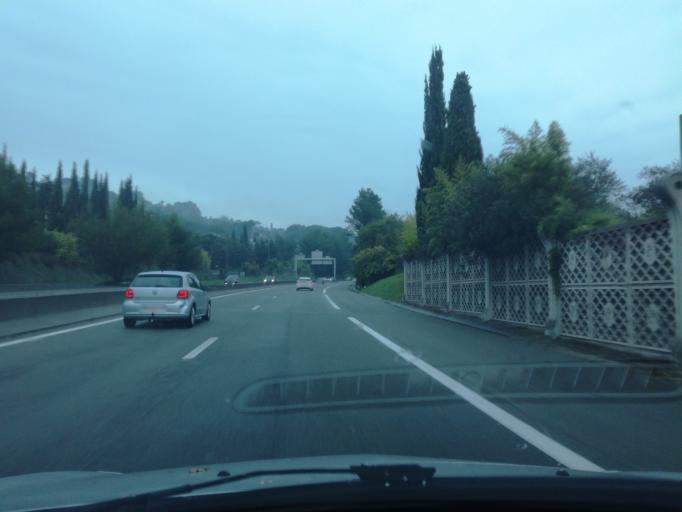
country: FR
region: Provence-Alpes-Cote d'Azur
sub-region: Departement des Alpes-Maritimes
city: Mougins
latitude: 43.5931
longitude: 7.0001
